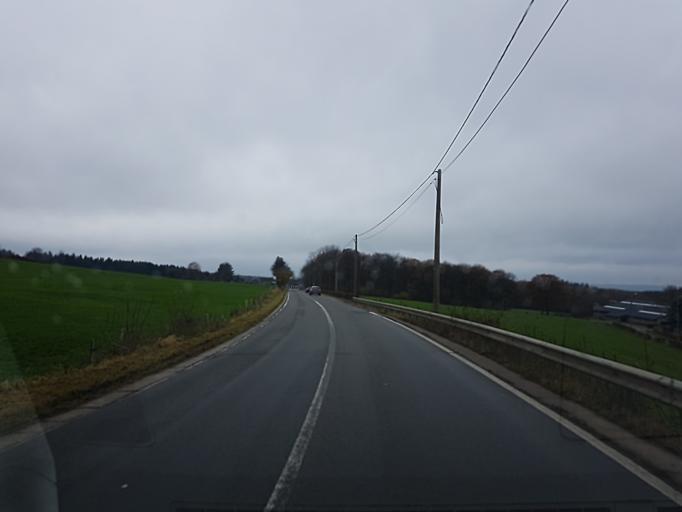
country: BE
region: Wallonia
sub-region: Province de Liege
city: Jalhay
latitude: 50.5705
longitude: 5.9293
